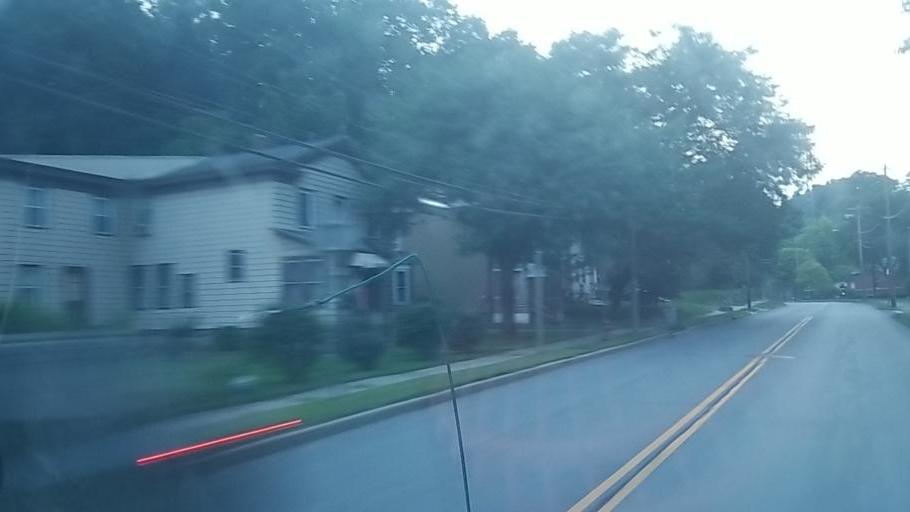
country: US
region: New York
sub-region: Montgomery County
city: Fonda
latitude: 42.9569
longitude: -74.3786
